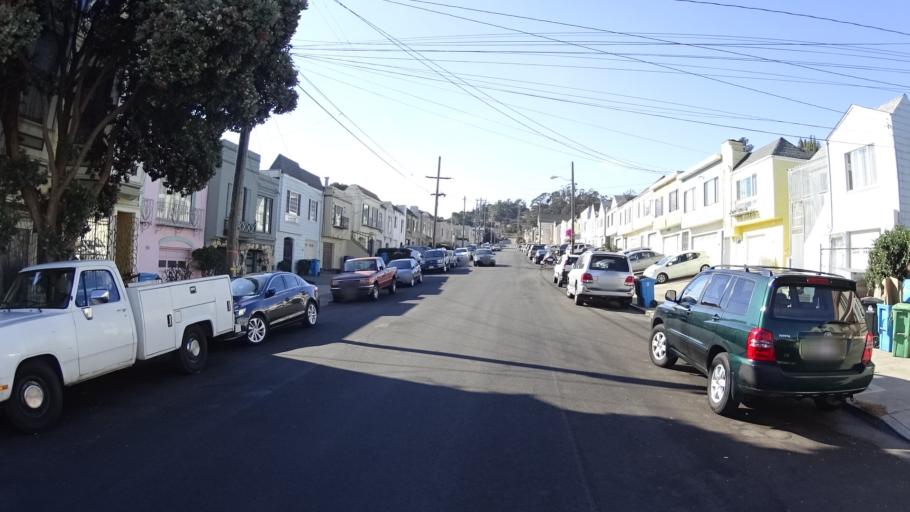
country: US
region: California
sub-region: San Mateo County
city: Brisbane
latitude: 37.7154
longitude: -122.4066
